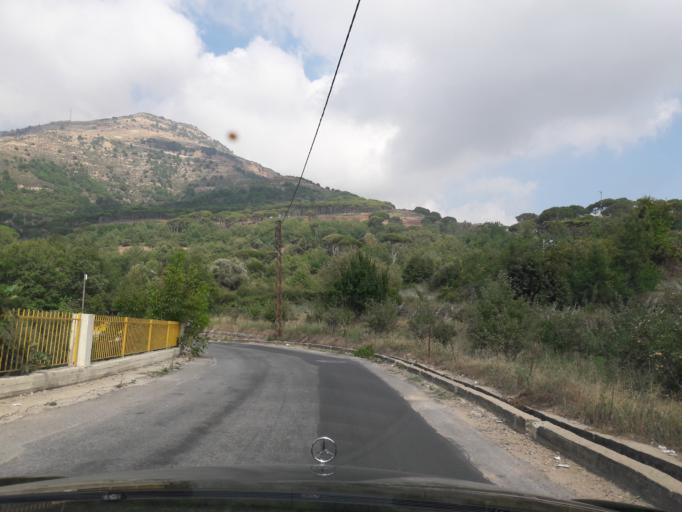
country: LB
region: Mont-Liban
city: Djounie
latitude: 33.9524
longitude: 35.7748
